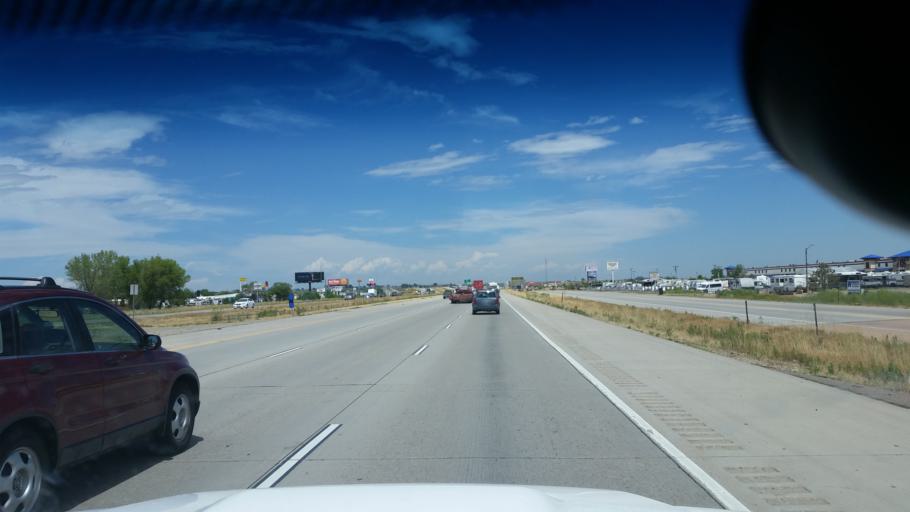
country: US
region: Colorado
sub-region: Weld County
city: Firestone
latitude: 40.1500
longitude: -104.9795
